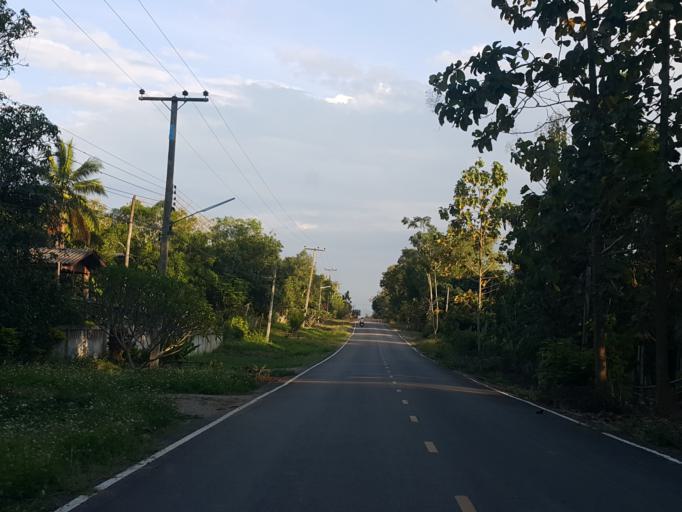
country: TH
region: Lampang
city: Lampang
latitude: 18.4191
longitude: 99.5541
